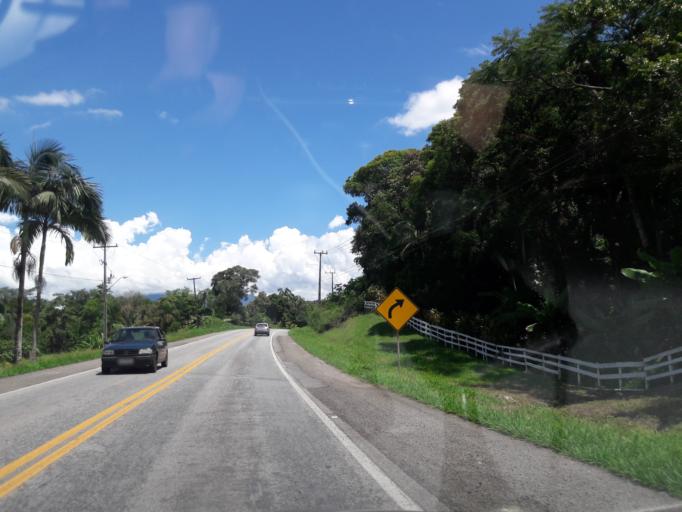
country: BR
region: Parana
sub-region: Antonina
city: Antonina
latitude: -25.4540
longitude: -48.8072
